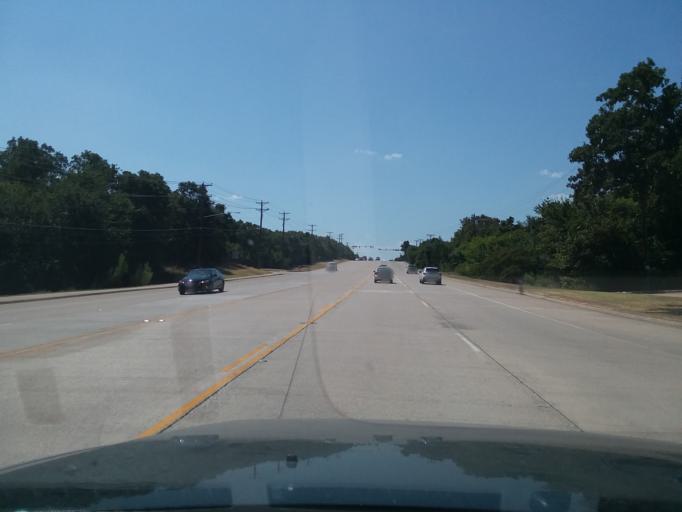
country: US
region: Texas
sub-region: Tarrant County
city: Euless
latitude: 32.8617
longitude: -97.1001
